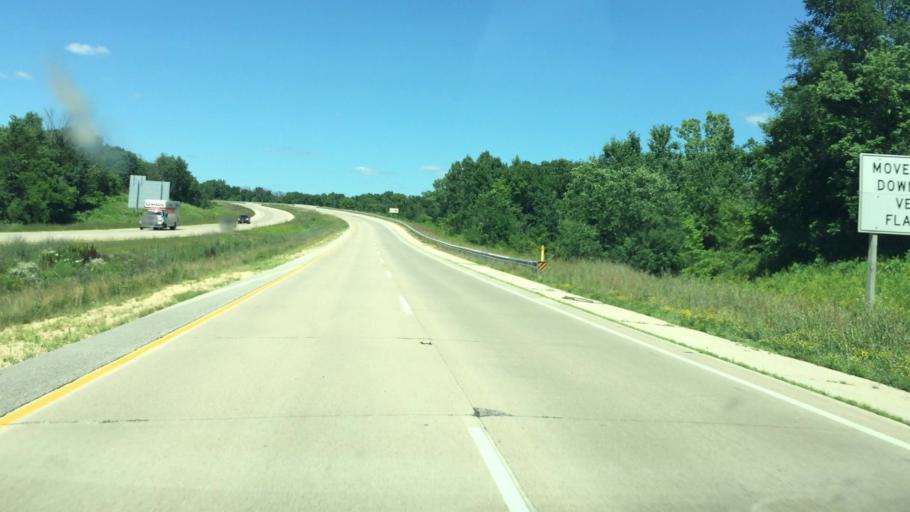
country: US
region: Illinois
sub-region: Jo Daviess County
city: East Dubuque
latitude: 42.5388
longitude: -90.6091
